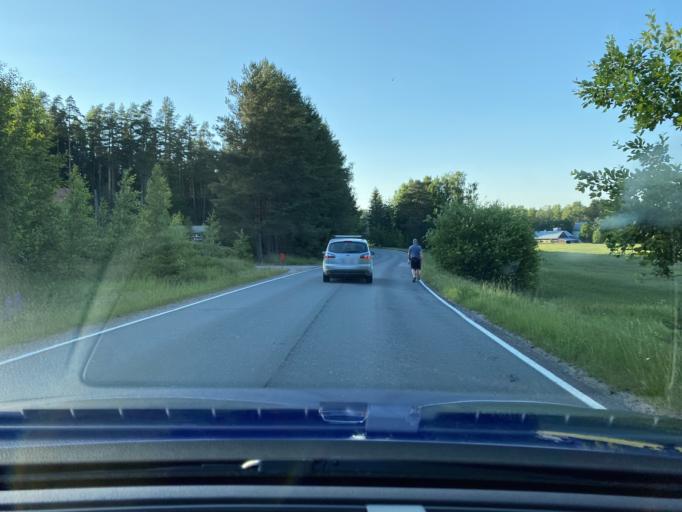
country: FI
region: Haeme
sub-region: Riihimaeki
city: Riihimaeki
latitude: 60.7223
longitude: 24.7041
